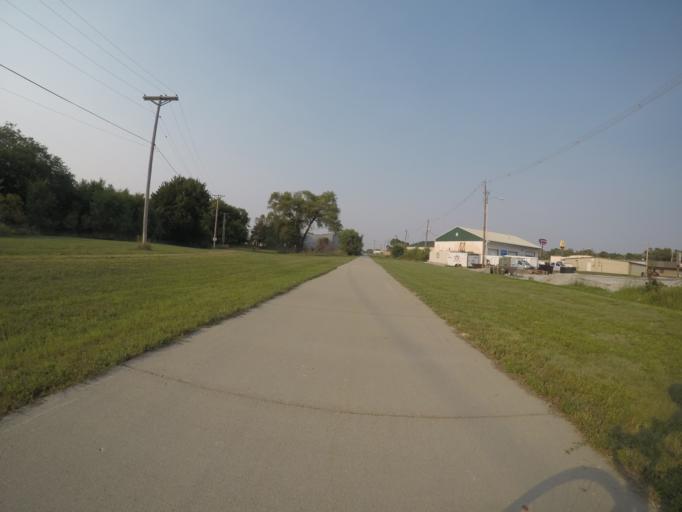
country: US
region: Nebraska
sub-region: Gage County
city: Beatrice
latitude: 40.2780
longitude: -96.7481
